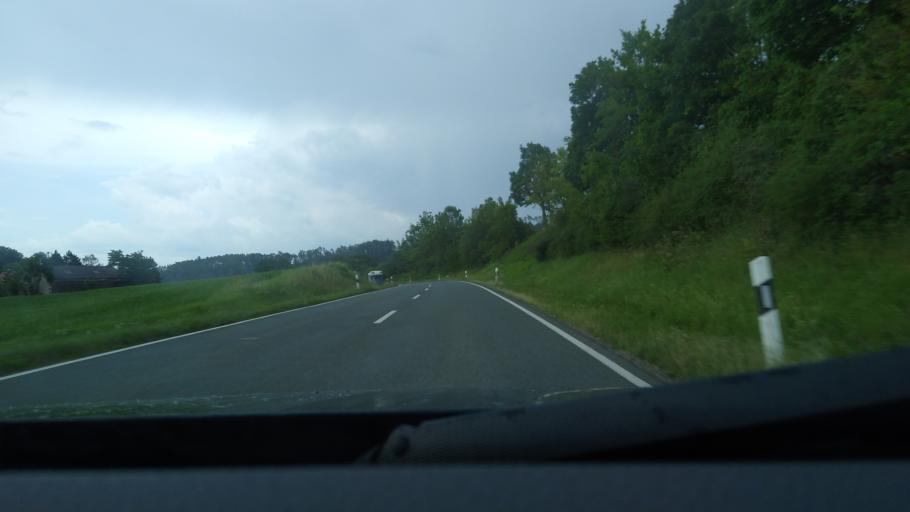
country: DE
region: Bavaria
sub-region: Regierungsbezirk Mittelfranken
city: Trautskirchen
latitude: 49.4586
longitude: 10.5753
